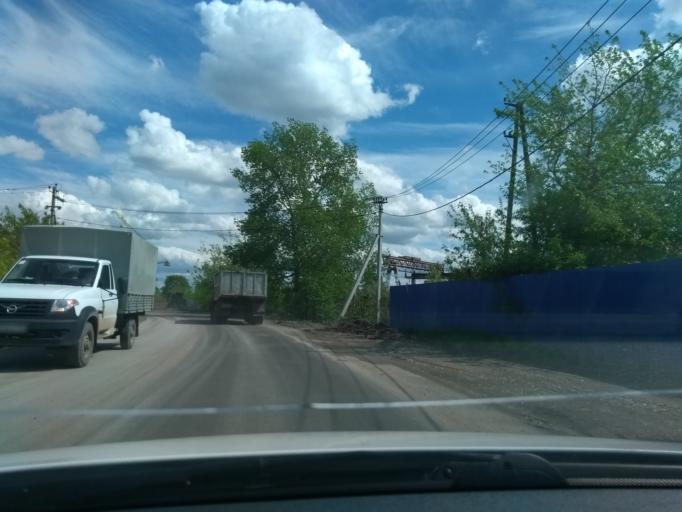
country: RU
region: Perm
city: Kondratovo
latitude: 58.0108
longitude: 56.0655
